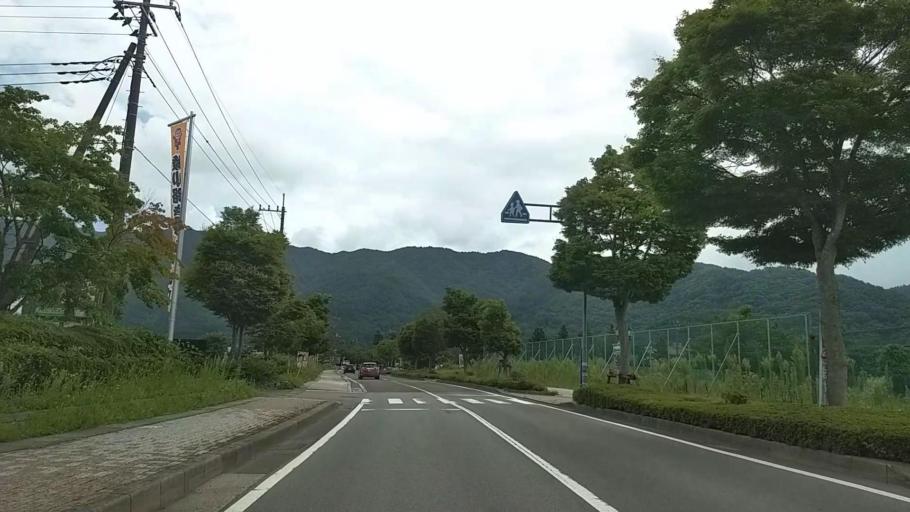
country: JP
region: Yamanashi
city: Fujikawaguchiko
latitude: 35.5241
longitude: 138.7664
